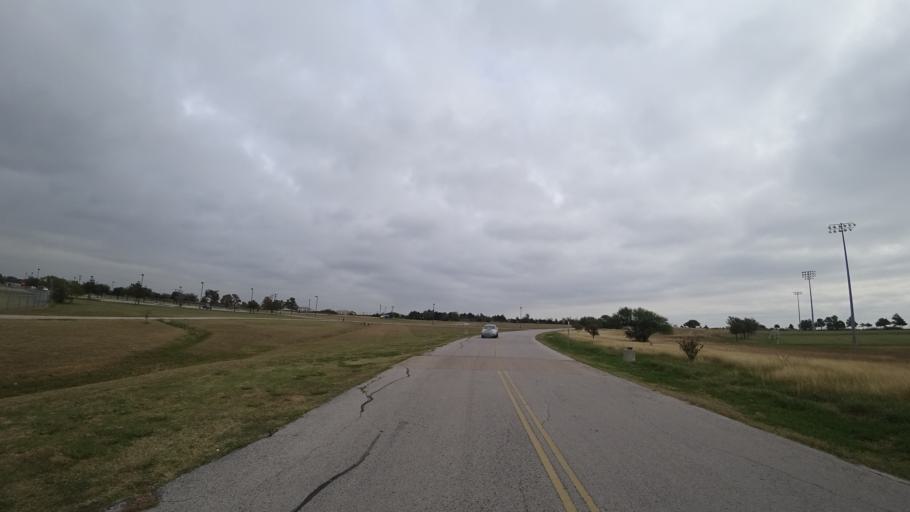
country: US
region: Texas
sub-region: Travis County
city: Pflugerville
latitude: 30.4146
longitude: -97.5982
